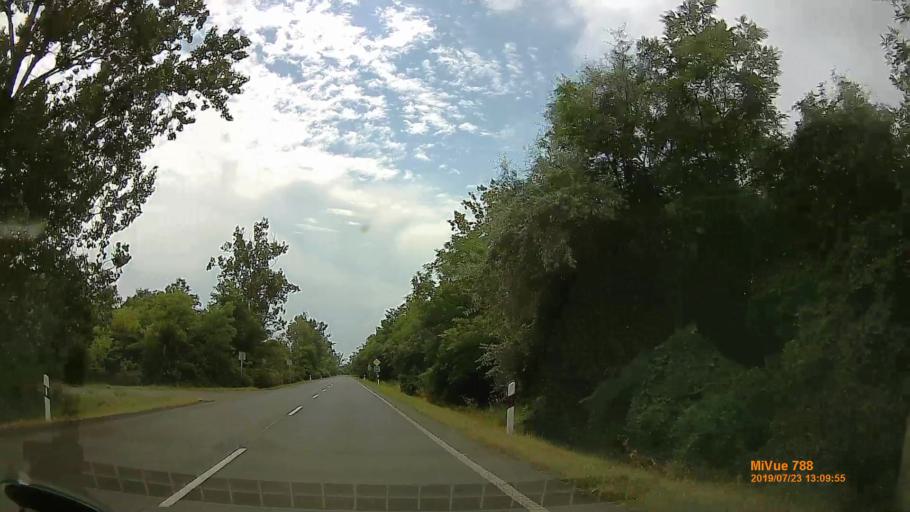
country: HU
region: Szabolcs-Szatmar-Bereg
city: Tiszavasvari
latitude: 47.9318
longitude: 21.2999
